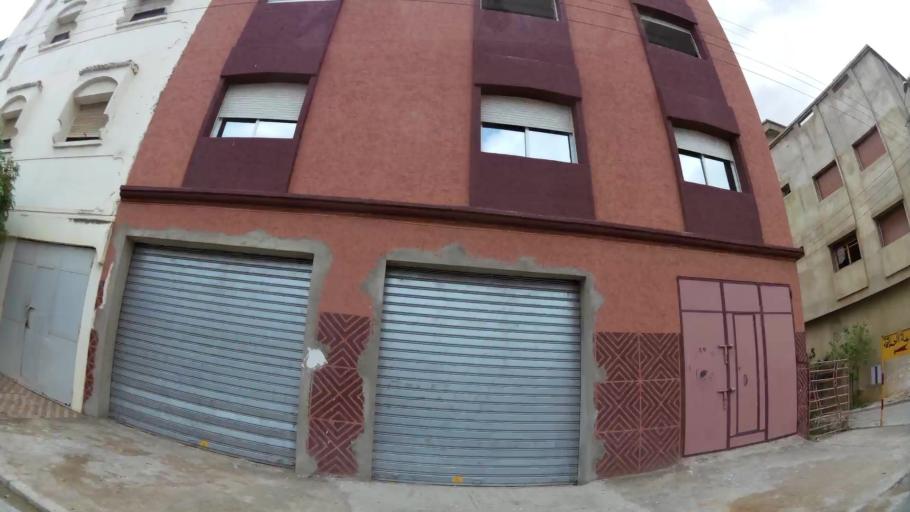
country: MA
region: Rabat-Sale-Zemmour-Zaer
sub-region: Khemisset
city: Tiflet
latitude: 33.8931
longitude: -6.3294
